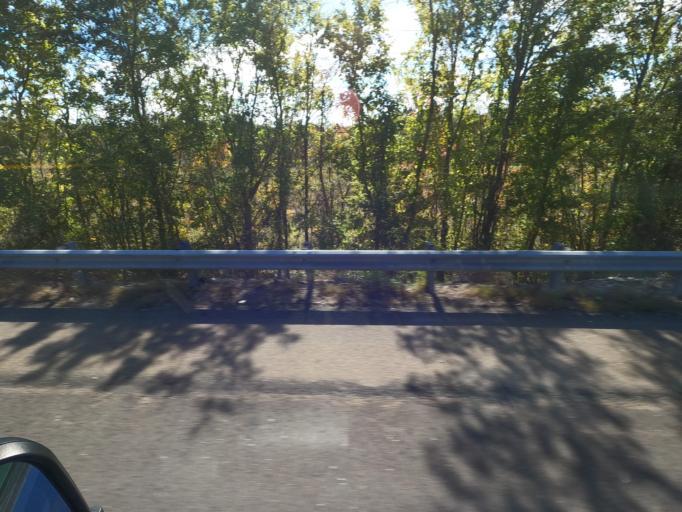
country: US
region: Tennessee
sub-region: Madison County
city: Jackson
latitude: 35.6480
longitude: -88.8971
